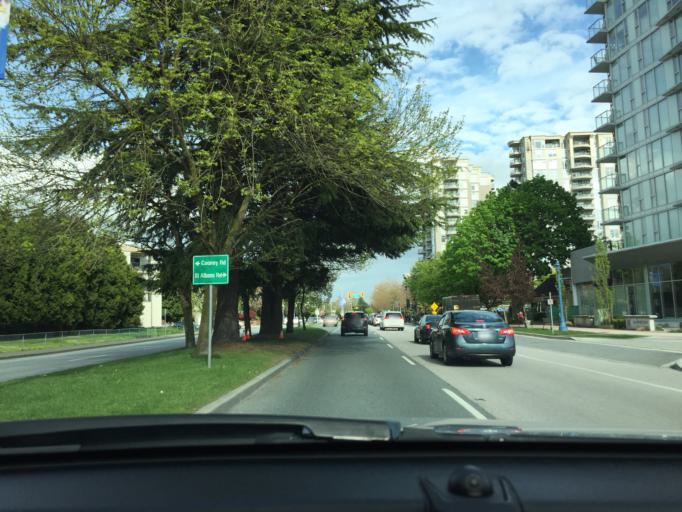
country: CA
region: British Columbia
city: Richmond
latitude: 49.1627
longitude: -123.1329
